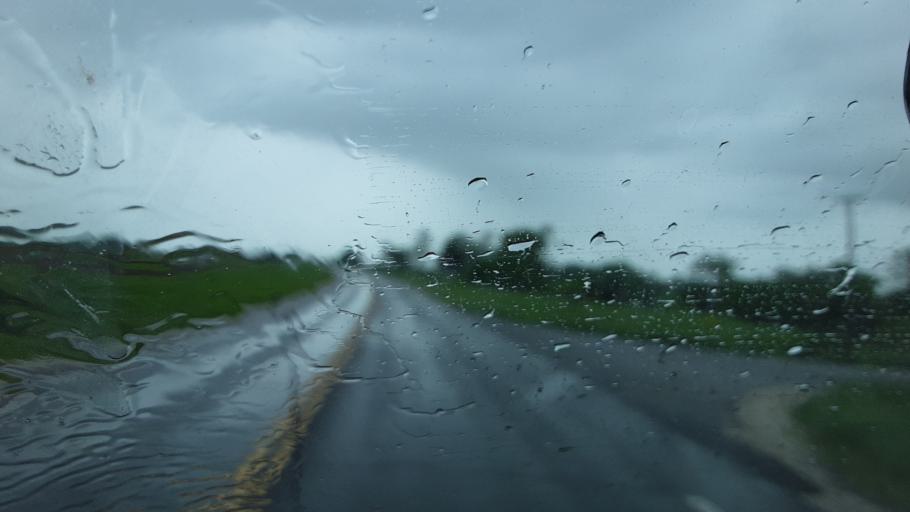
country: US
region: Missouri
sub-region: Monroe County
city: Paris
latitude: 39.4798
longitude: -92.1755
